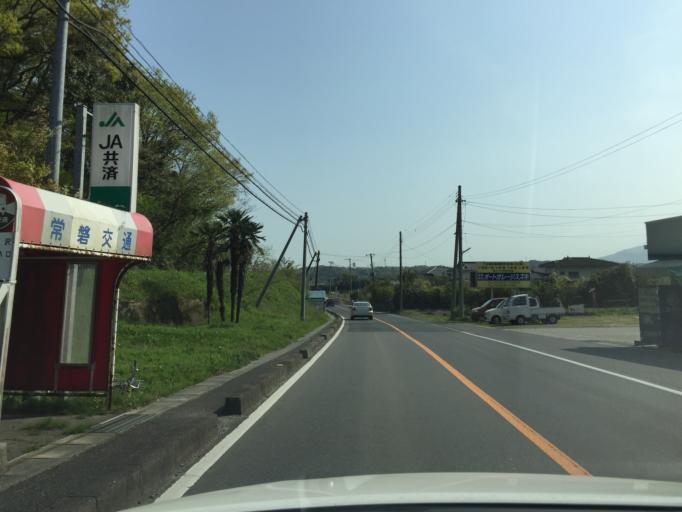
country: JP
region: Fukushima
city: Iwaki
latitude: 37.0934
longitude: 140.8735
